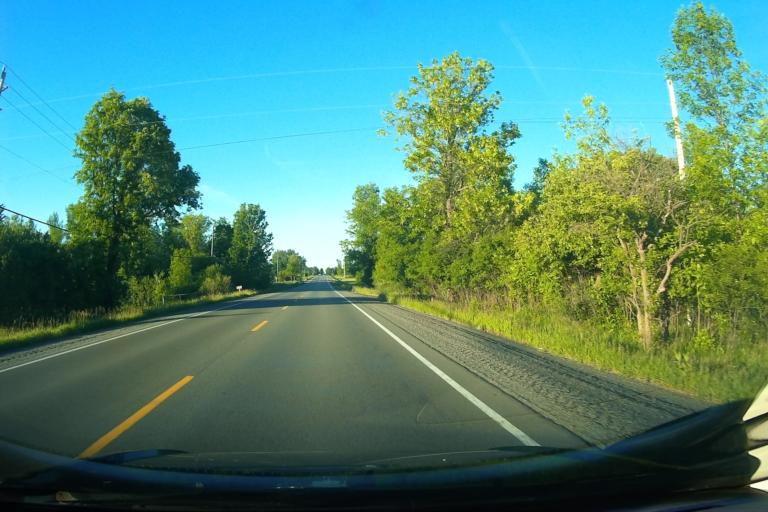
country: CA
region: Ontario
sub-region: Lanark County
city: Smiths Falls
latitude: 44.9786
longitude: -75.7343
